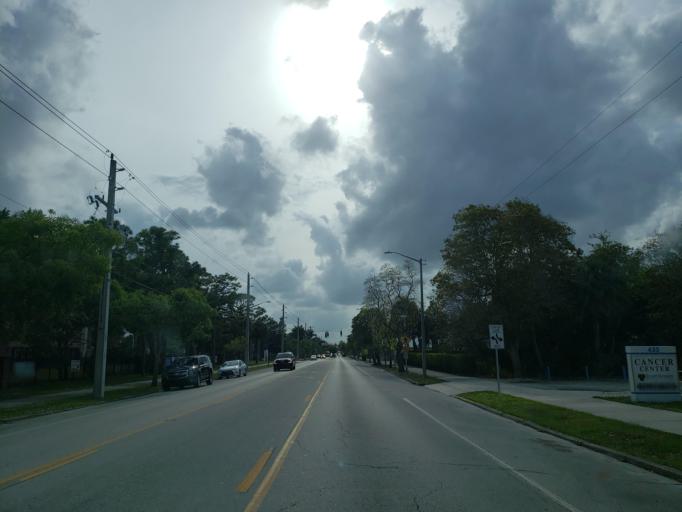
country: US
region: Florida
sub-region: Martin County
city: Stuart
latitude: 27.1975
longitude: -80.2455
